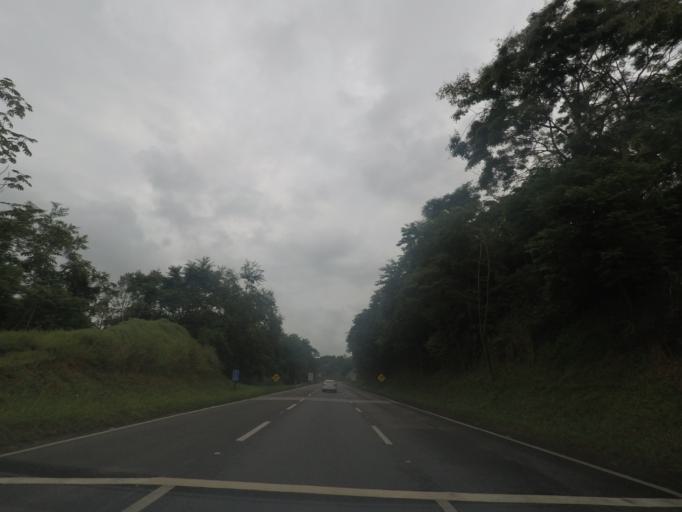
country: BR
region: Sao Paulo
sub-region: Cajati
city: Cajati
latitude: -24.7833
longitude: -48.1782
